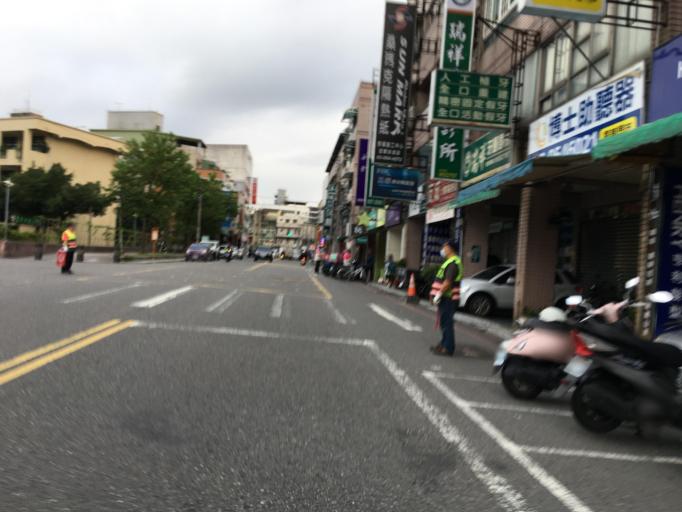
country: TW
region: Taiwan
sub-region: Yilan
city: Yilan
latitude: 24.6717
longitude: 121.7678
